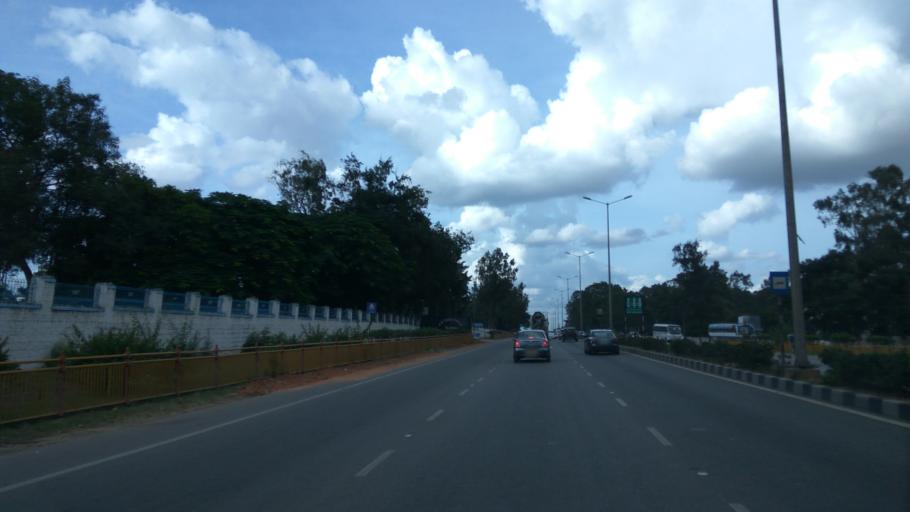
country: IN
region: Karnataka
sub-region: Bangalore Urban
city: Yelahanka
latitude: 13.1302
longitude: 77.6147
